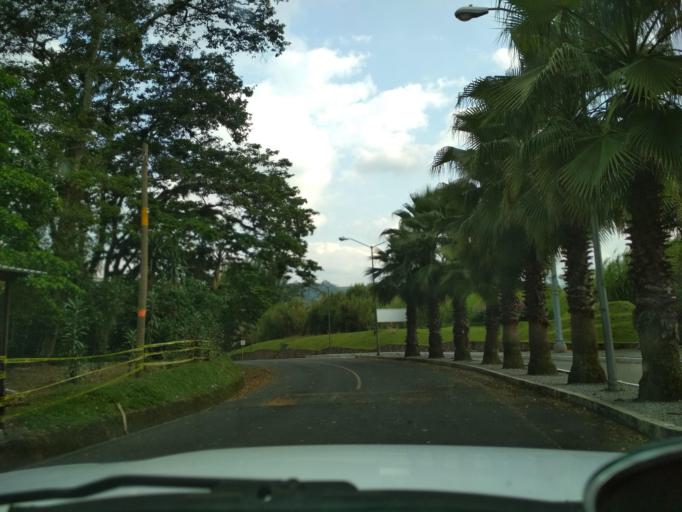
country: MX
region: Veracruz
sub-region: Fortin
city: Monte Salas
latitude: 18.9150
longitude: -97.0265
